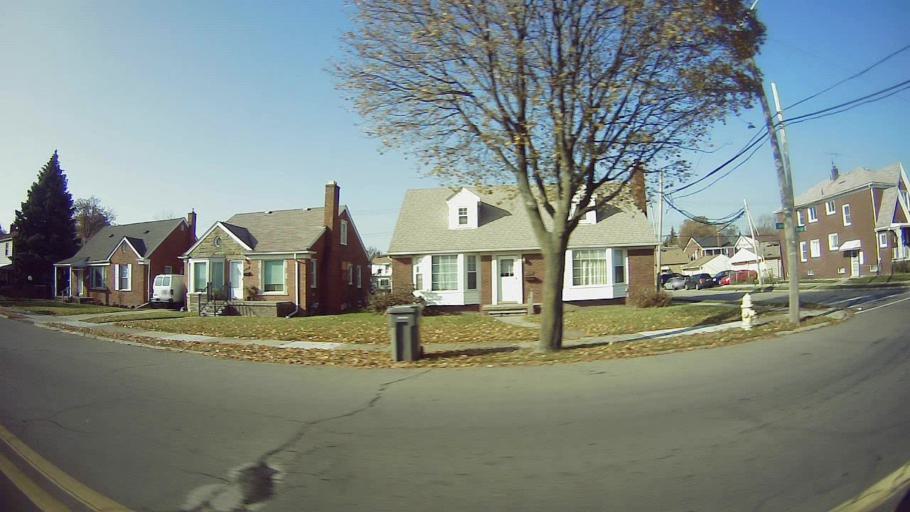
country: US
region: Michigan
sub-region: Wayne County
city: Dearborn
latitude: 42.3405
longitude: -83.1669
